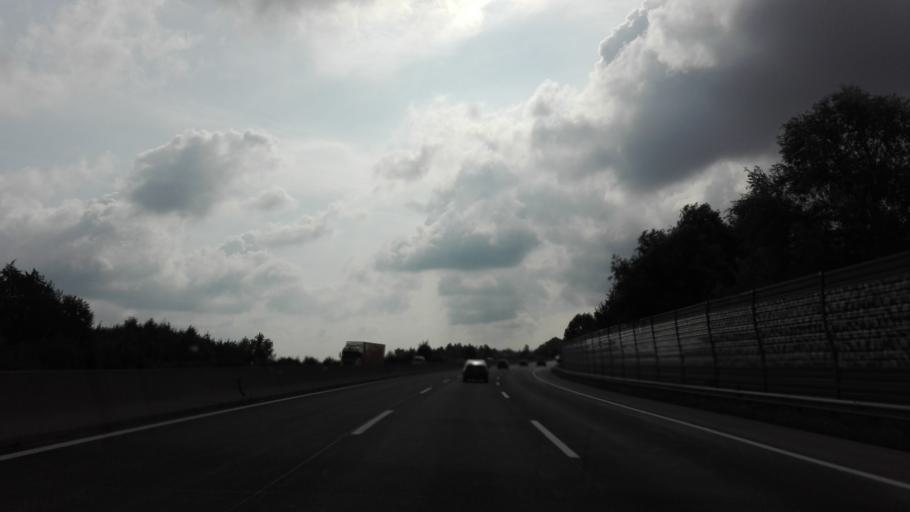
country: AT
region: Lower Austria
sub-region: Politischer Bezirk Amstetten
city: Strengberg
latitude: 48.1185
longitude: 14.6473
